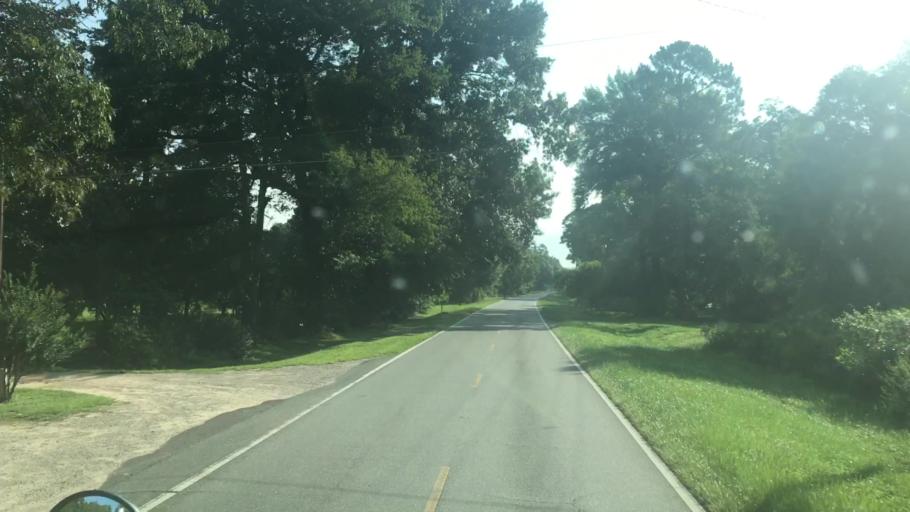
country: US
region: Florida
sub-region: Gadsden County
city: Quincy
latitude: 30.6601
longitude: -84.5619
